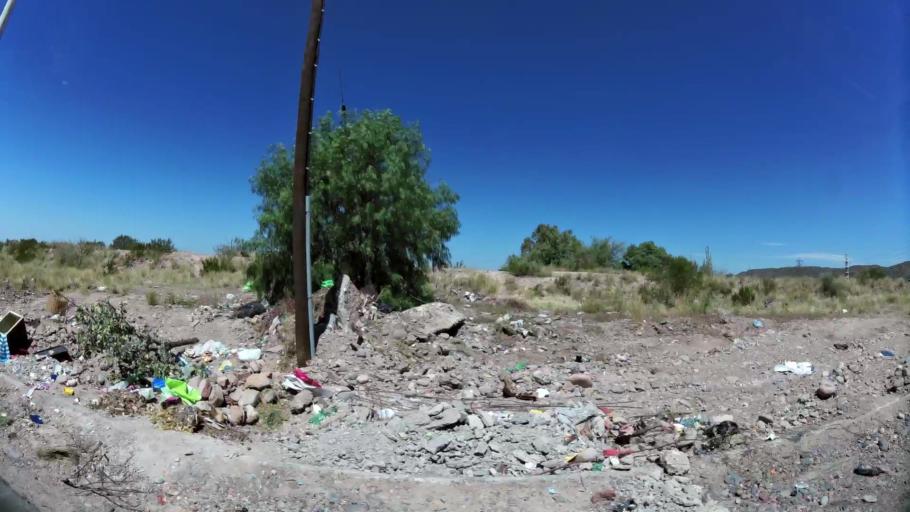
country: AR
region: Mendoza
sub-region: Departamento de Godoy Cruz
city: Godoy Cruz
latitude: -32.9495
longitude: -68.8724
